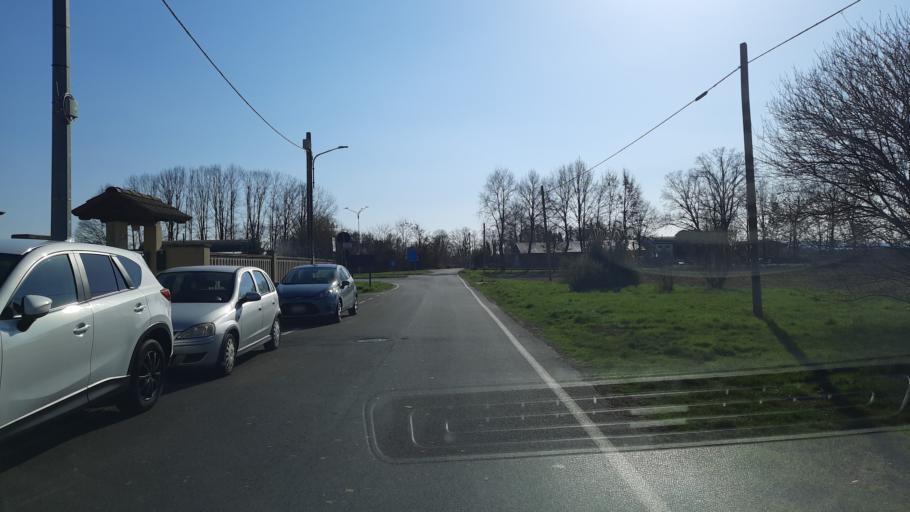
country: IT
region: Piedmont
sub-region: Provincia di Vercelli
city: Costanzana
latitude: 45.2322
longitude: 8.3701
